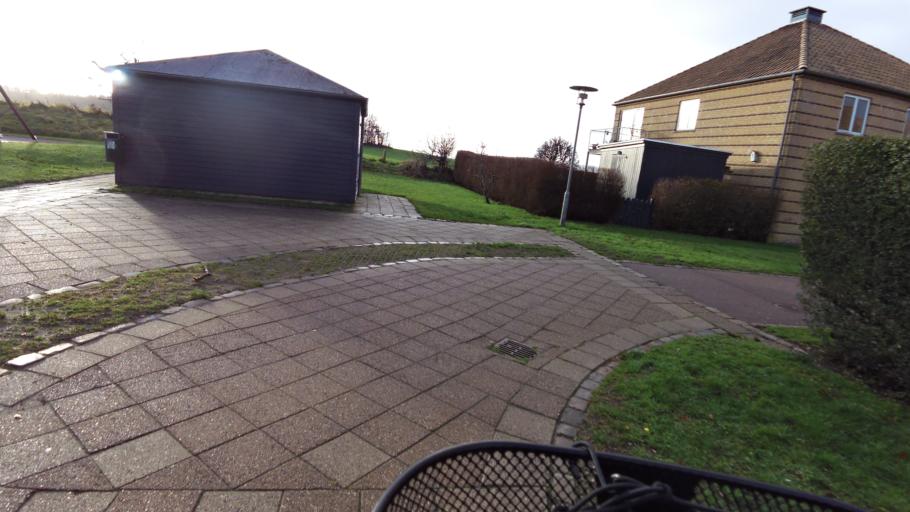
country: DK
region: Central Jutland
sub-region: Arhus Kommune
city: Marslet
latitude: 56.1022
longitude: 10.1686
